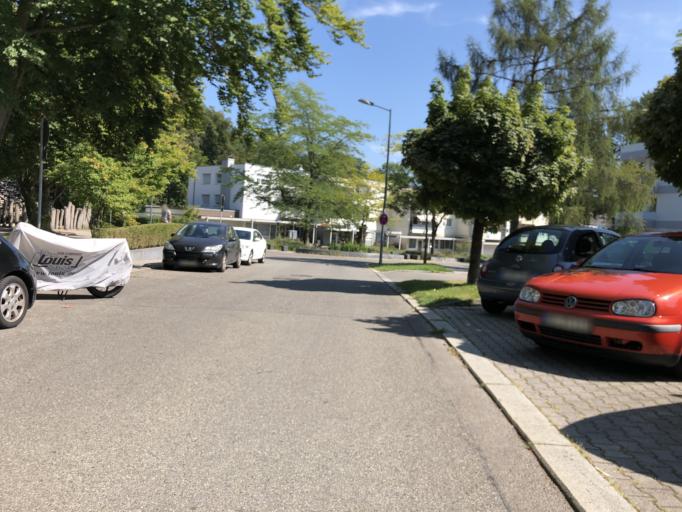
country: DE
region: Baden-Wuerttemberg
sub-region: Regierungsbezirk Stuttgart
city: Sindelfingen
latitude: 48.7310
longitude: 9.0015
